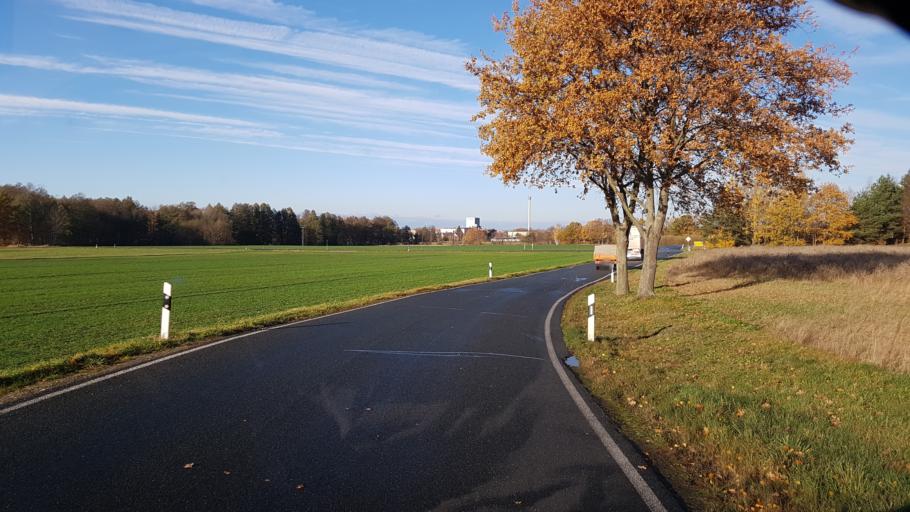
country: DE
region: Brandenburg
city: Ortrand
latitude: 51.3615
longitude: 13.7655
